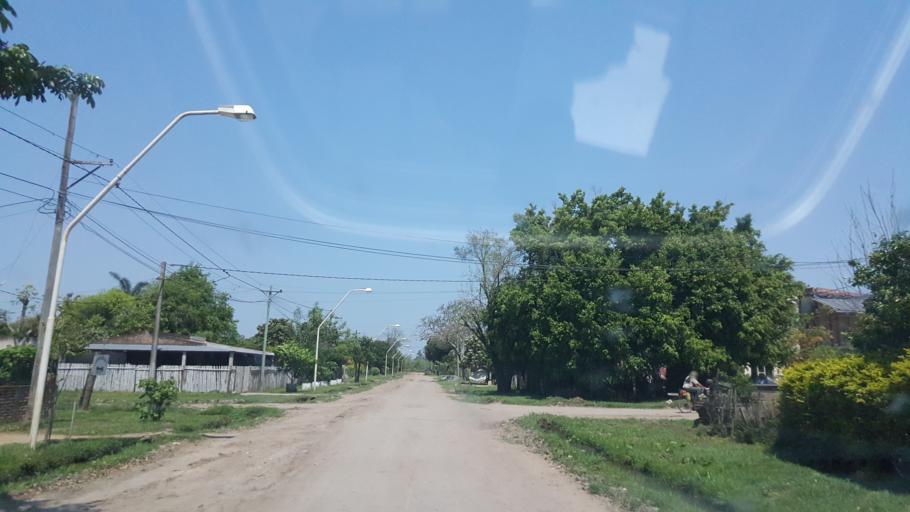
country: AR
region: Corrientes
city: Ita Ibate
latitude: -27.4254
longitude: -57.3291
